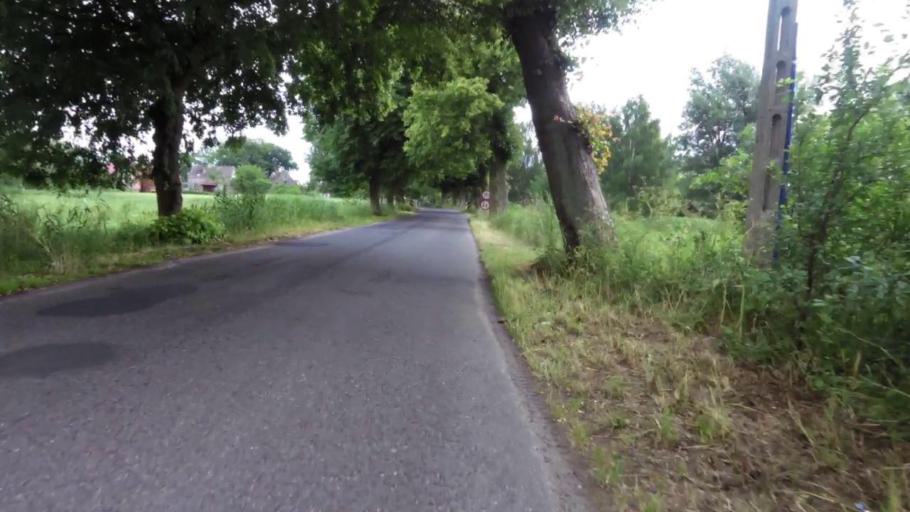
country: PL
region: West Pomeranian Voivodeship
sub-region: Powiat goleniowski
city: Stepnica
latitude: 53.6597
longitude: 14.6125
